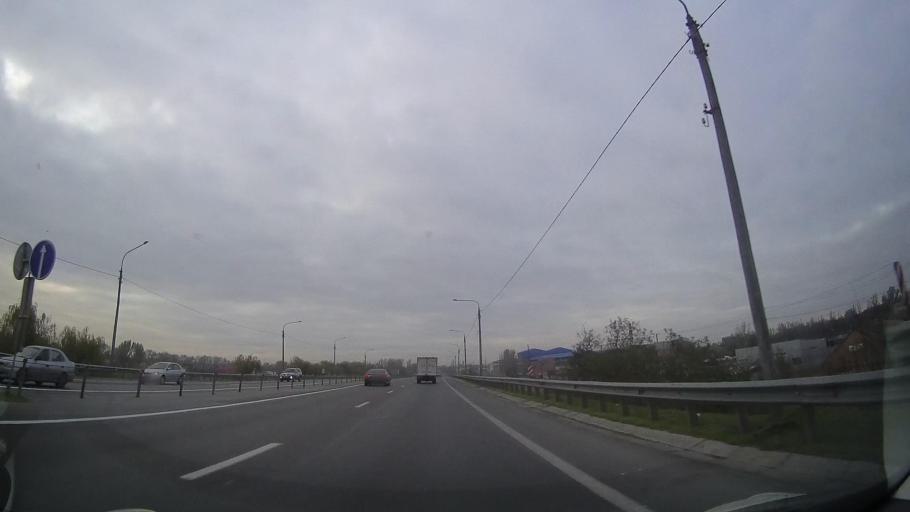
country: RU
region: Rostov
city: Bataysk
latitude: 47.1195
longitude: 39.7707
